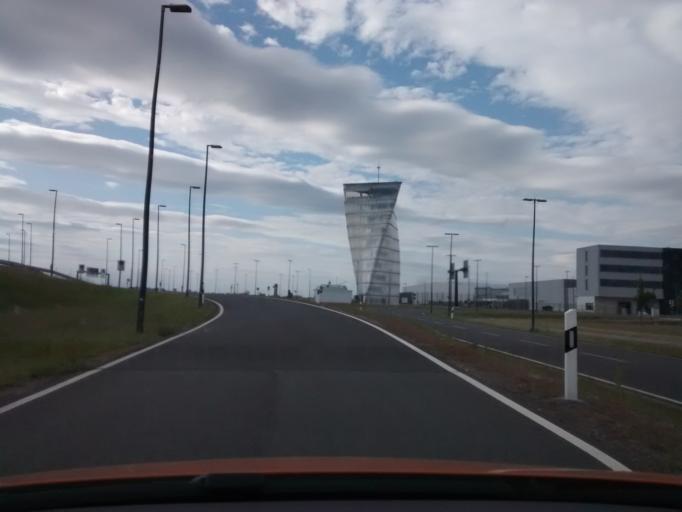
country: DE
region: Brandenburg
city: Schonefeld
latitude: 52.3665
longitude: 13.5169
